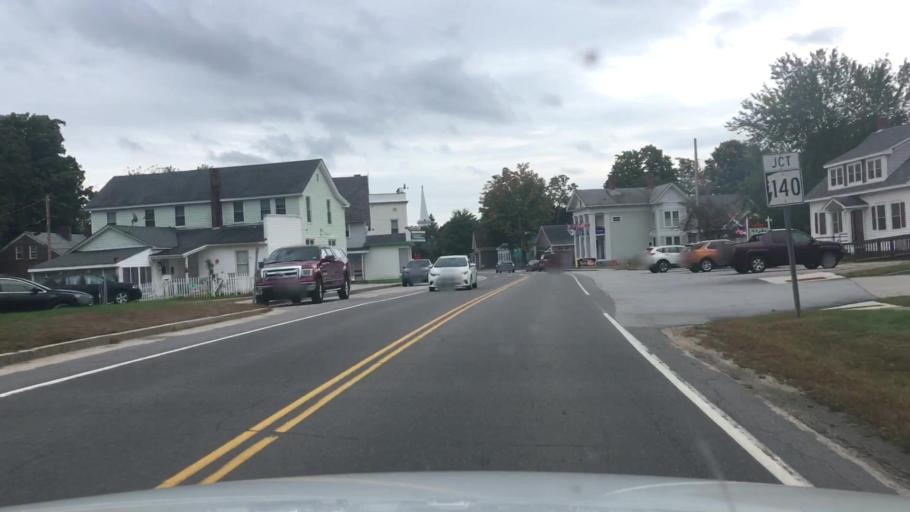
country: US
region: New Hampshire
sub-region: Strafford County
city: New Durham
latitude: 43.4574
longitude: -71.2219
